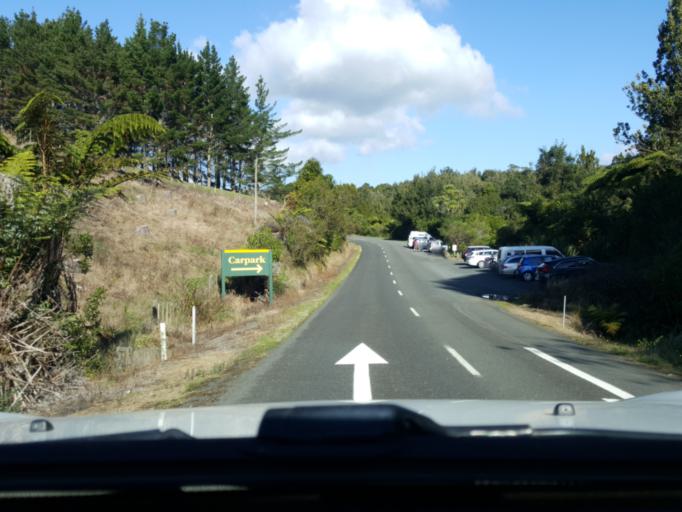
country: NZ
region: Waikato
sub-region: Waikato District
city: Raglan
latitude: -37.9066
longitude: 174.9013
